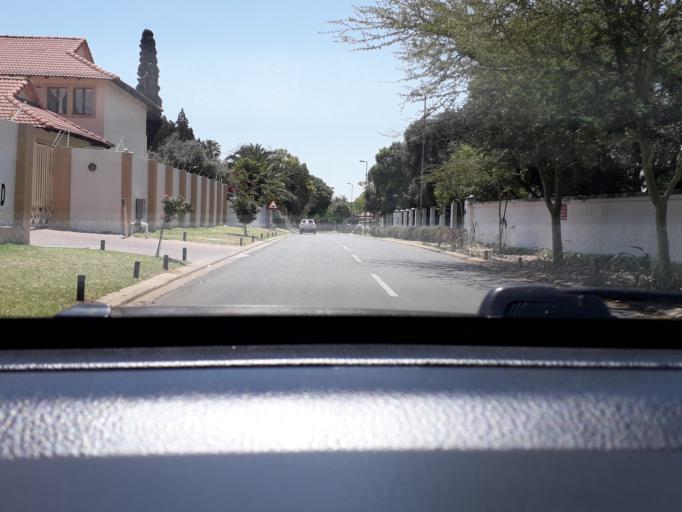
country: ZA
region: Gauteng
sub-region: City of Johannesburg Metropolitan Municipality
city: Midrand
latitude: -26.0501
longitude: 28.0629
